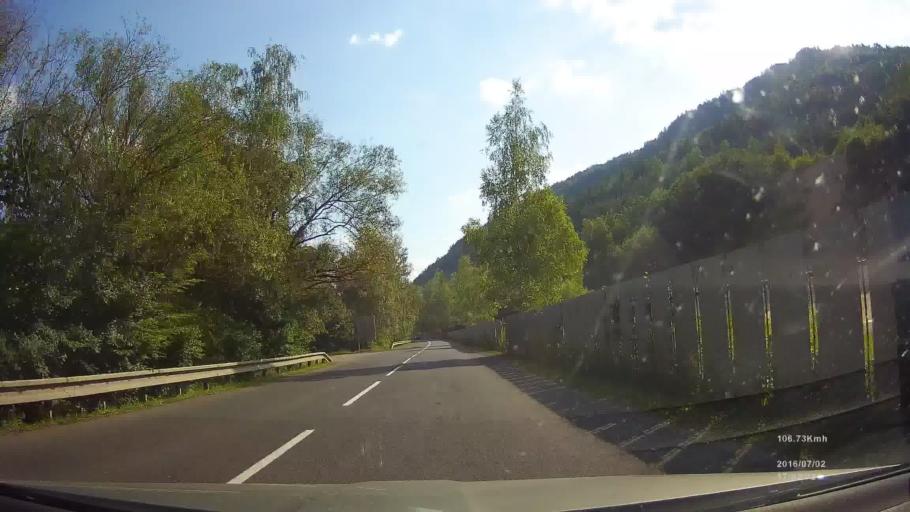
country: SK
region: Kosicky
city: Gelnica
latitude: 48.8855
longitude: 21.0036
